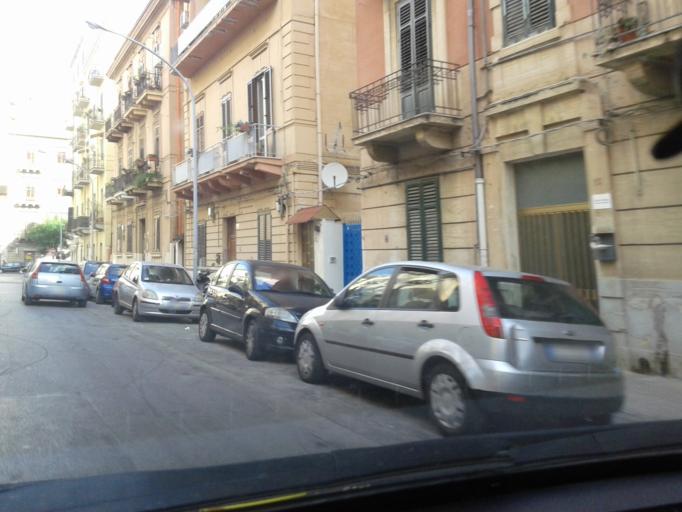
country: IT
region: Sicily
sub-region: Palermo
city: Palermo
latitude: 38.1057
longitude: 13.3391
